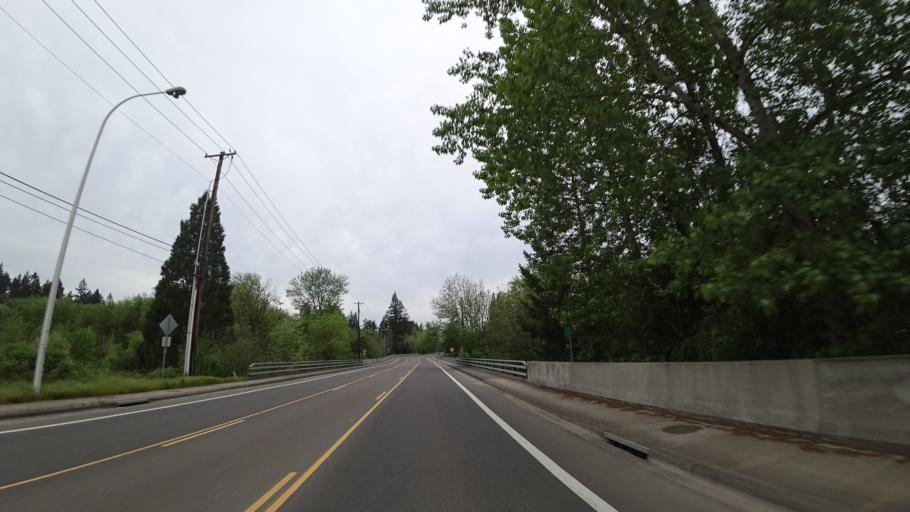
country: US
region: Oregon
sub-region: Washington County
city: Hillsboro
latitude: 45.5084
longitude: -122.9331
